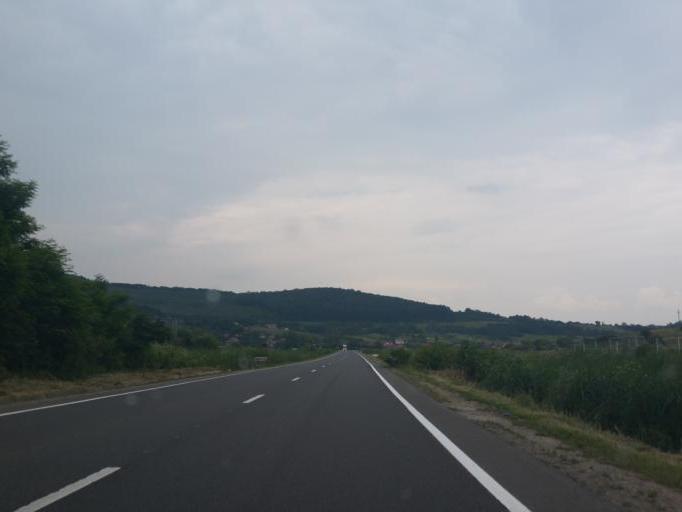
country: RO
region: Cluj
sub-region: Comuna Sanpaul
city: Sanpaul
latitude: 46.8897
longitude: 23.4121
